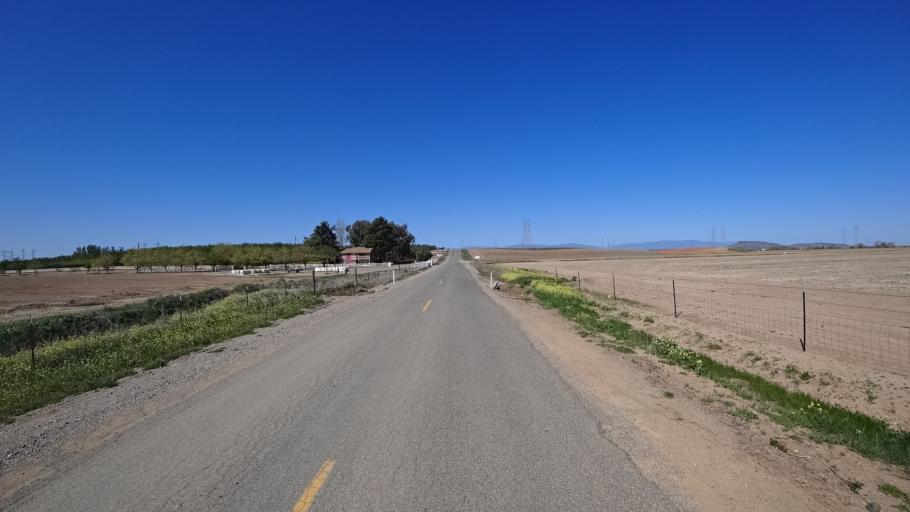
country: US
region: California
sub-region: Glenn County
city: Orland
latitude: 39.6974
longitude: -122.2602
